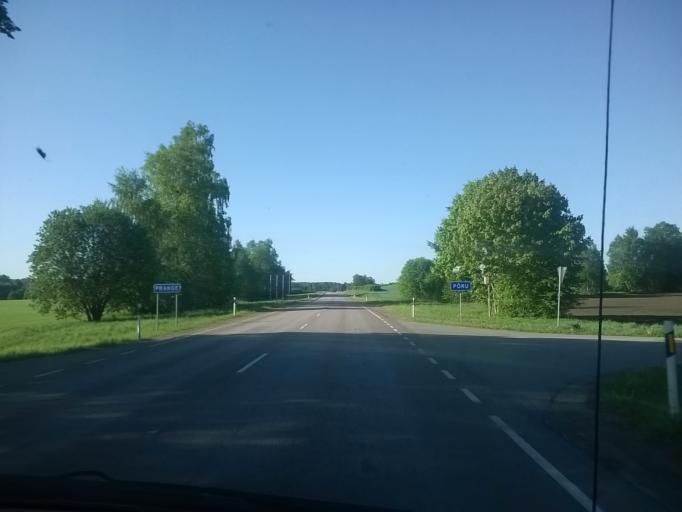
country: EE
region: Valgamaa
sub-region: Torva linn
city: Torva
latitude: 58.0519
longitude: 26.1929
